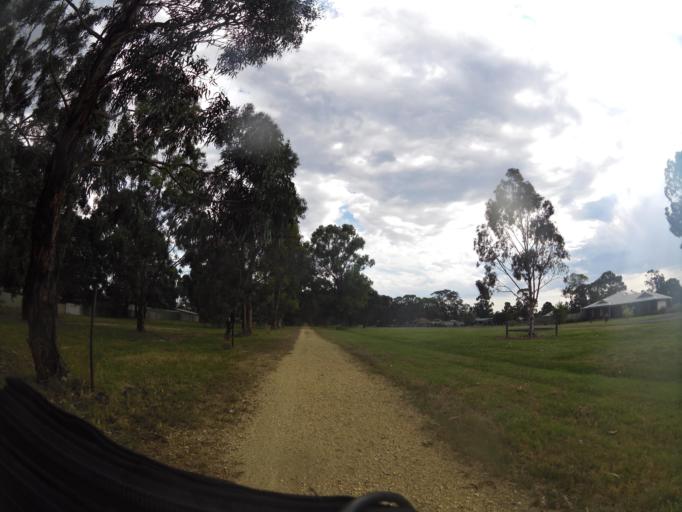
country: AU
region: Victoria
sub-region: Latrobe
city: Traralgon
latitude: -38.0569
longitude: 146.6272
